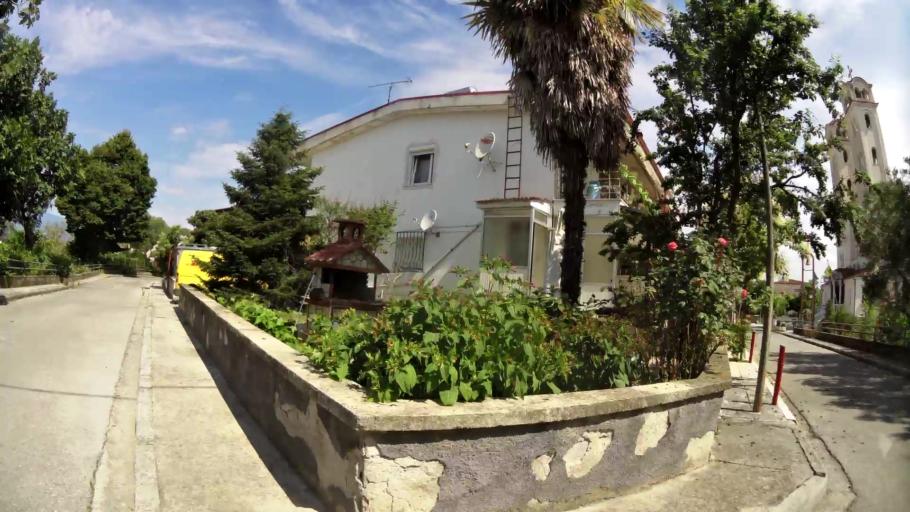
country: GR
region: Central Macedonia
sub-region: Nomos Pierias
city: Katerini
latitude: 40.2639
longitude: 22.4943
